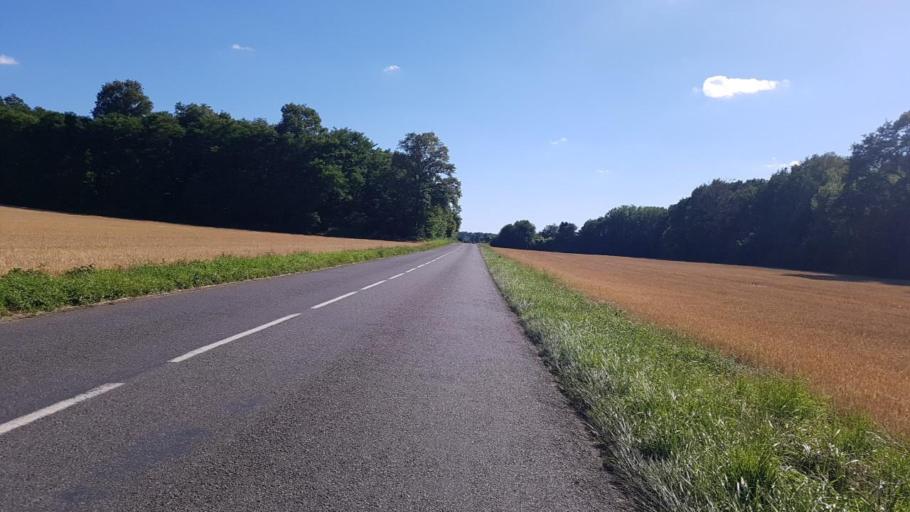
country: FR
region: Ile-de-France
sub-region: Departement de Seine-et-Marne
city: Esbly
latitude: 48.9185
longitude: 2.7917
